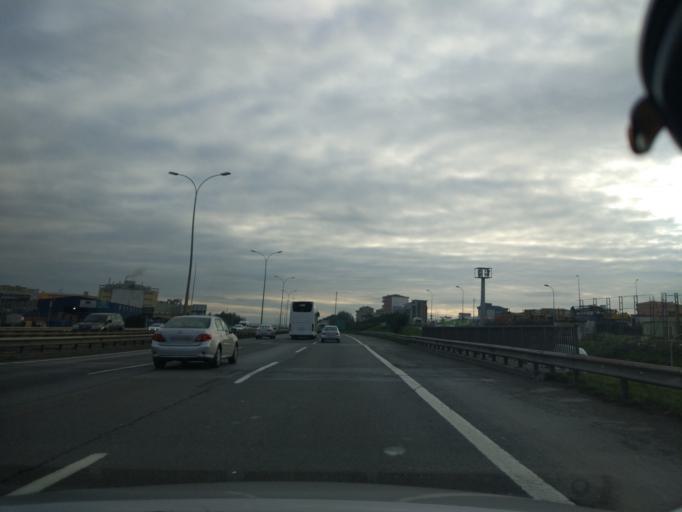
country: TR
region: Istanbul
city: Samandira
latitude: 40.9905
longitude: 29.1791
